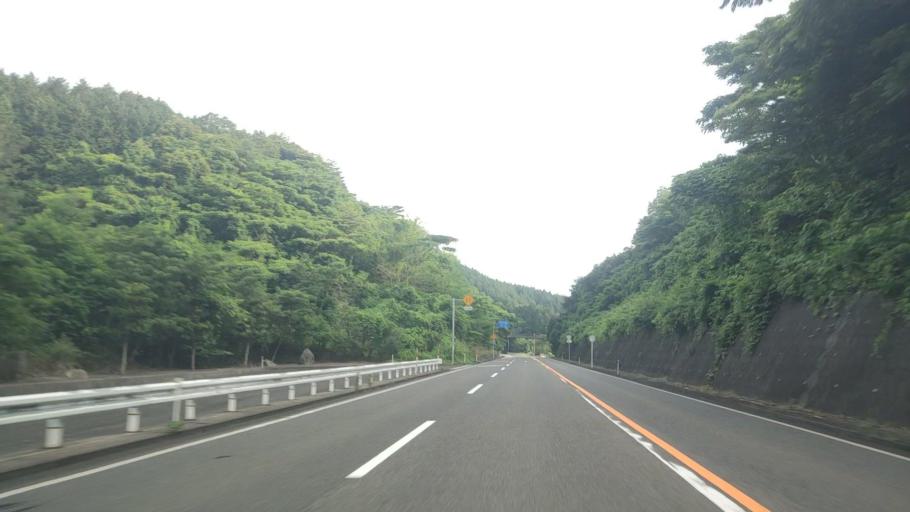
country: JP
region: Tottori
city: Kurayoshi
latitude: 35.3480
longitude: 133.7496
